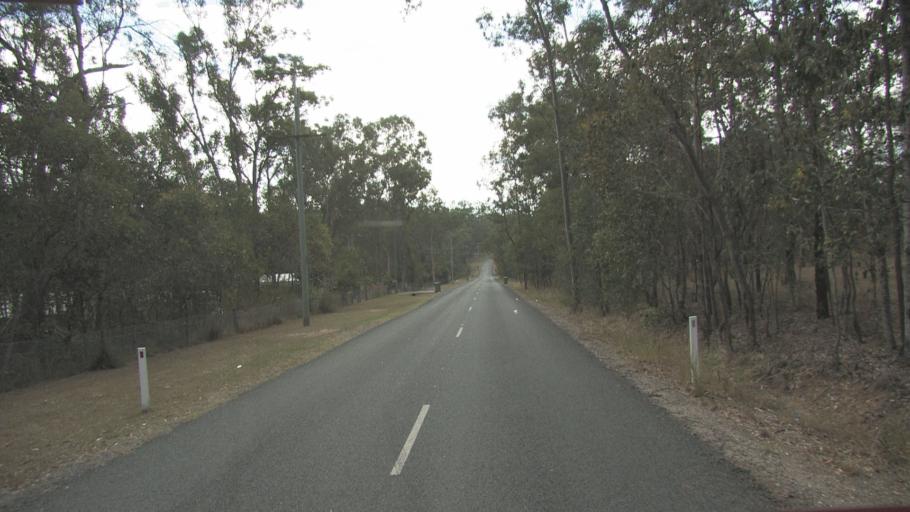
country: AU
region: Queensland
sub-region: Logan
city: North Maclean
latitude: -27.7632
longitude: 152.9704
